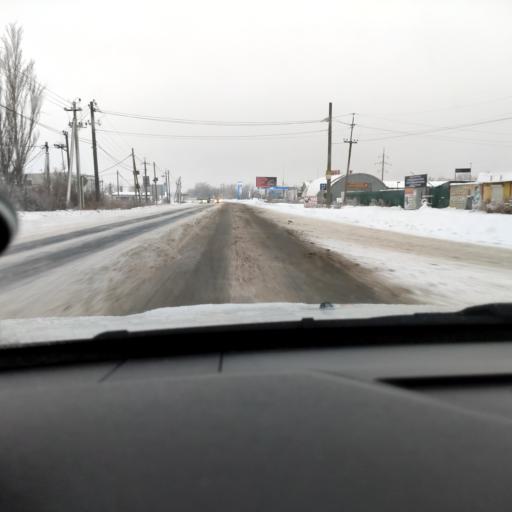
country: RU
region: Samara
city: Smyshlyayevka
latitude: 53.2529
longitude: 50.4753
